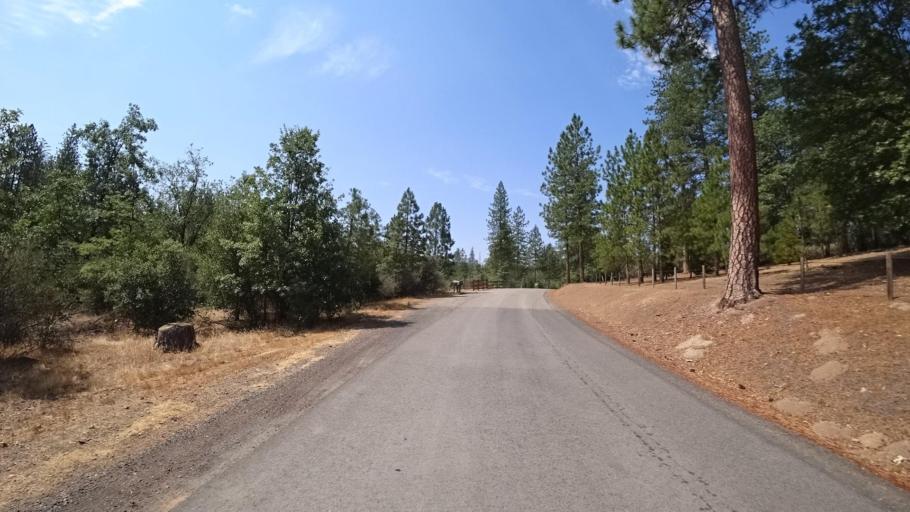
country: US
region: California
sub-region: Mariposa County
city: Midpines
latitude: 37.6975
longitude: -120.1000
